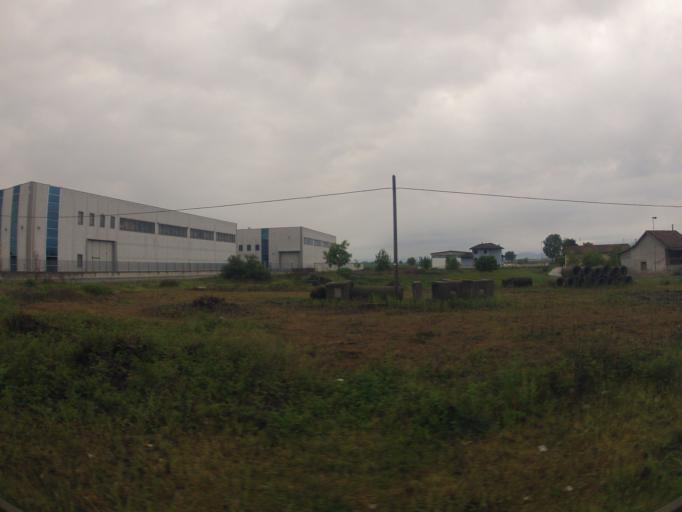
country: IT
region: Piedmont
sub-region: Provincia di Cuneo
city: Faule
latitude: 44.8011
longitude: 7.5805
